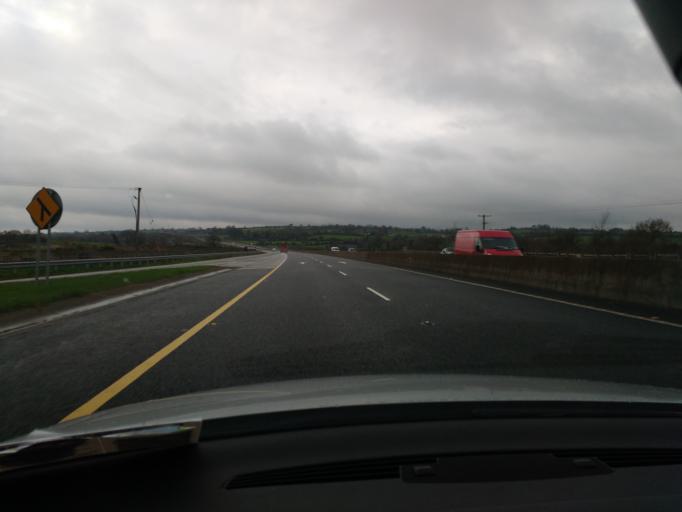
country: IE
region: Munster
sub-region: North Tipperary
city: Nenagh
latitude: 52.8452
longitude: -8.2531
